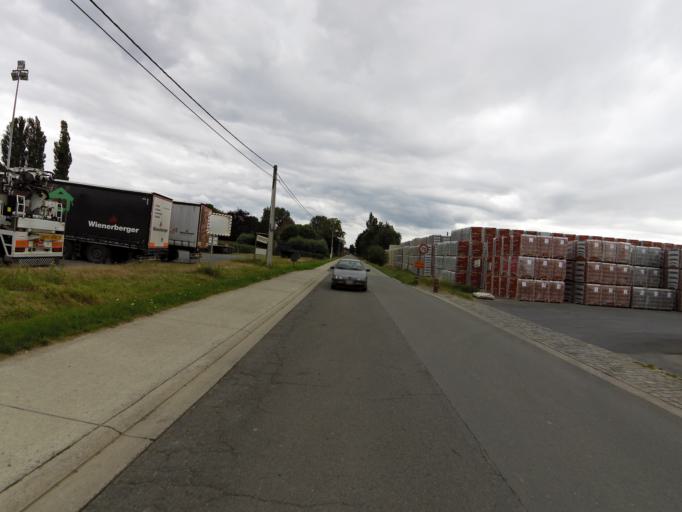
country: BE
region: Flanders
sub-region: Provincie West-Vlaanderen
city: Kortemark
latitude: 51.0191
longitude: 3.0462
